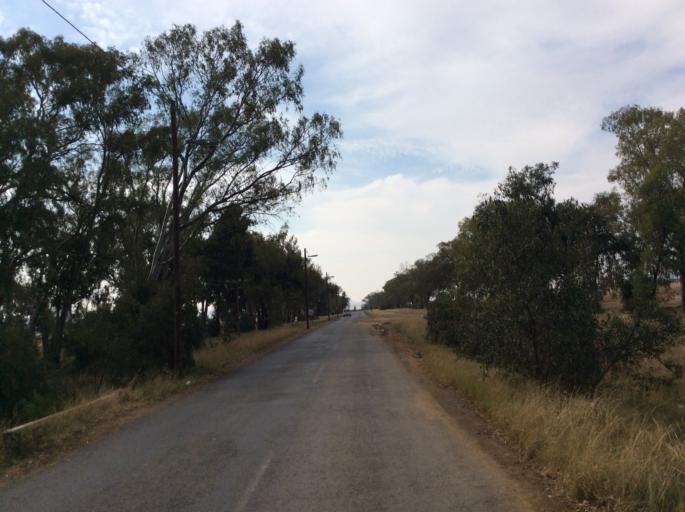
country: ZA
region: Orange Free State
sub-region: Xhariep District Municipality
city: Dewetsdorp
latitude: -29.5757
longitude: 26.6791
